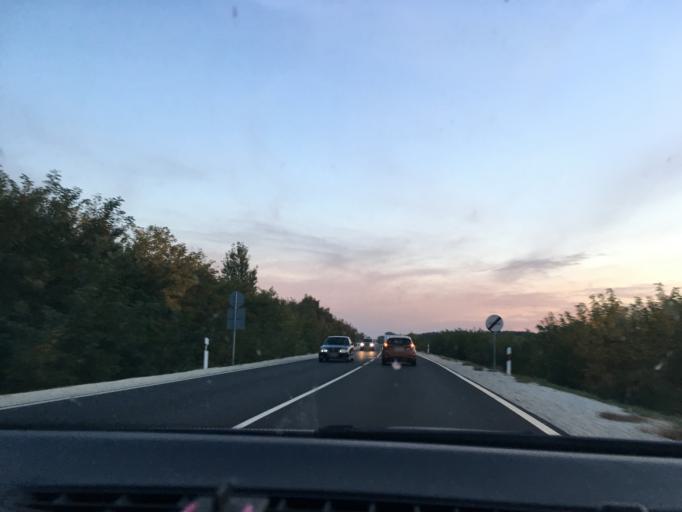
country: HU
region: Hajdu-Bihar
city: Debrecen
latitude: 47.5965
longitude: 21.6535
